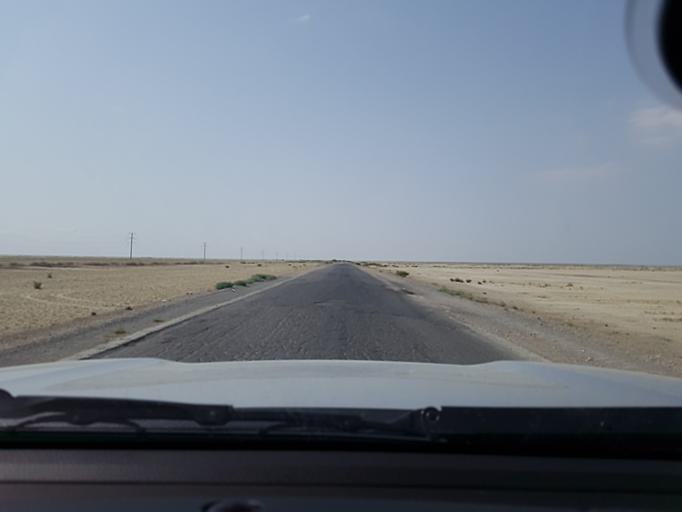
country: TM
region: Balkan
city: Gumdag
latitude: 38.9891
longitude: 54.5869
